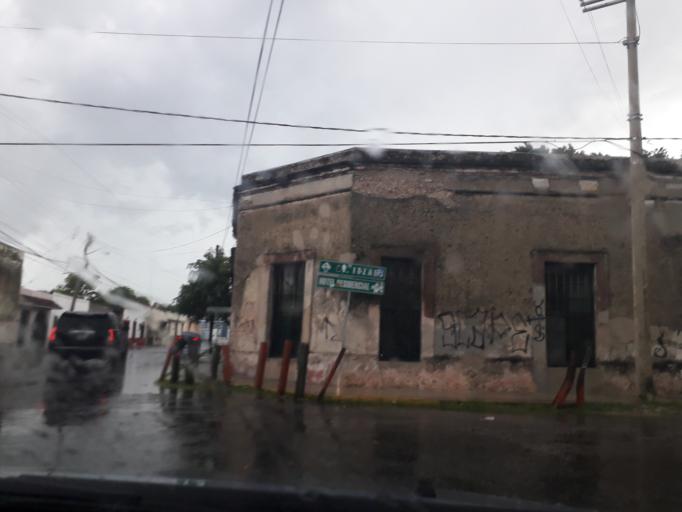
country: MX
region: Yucatan
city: Merida
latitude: 20.9691
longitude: -89.6339
